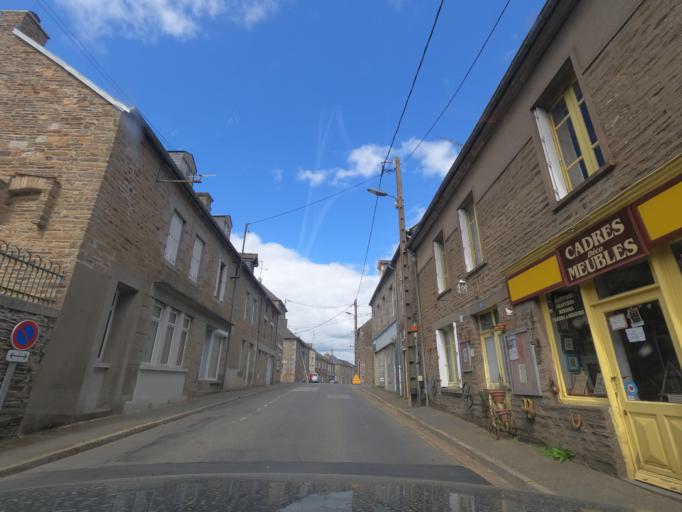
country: FR
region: Pays de la Loire
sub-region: Departement de la Mayenne
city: Fougerolles-du-Plessis
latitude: 48.4750
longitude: -0.9718
